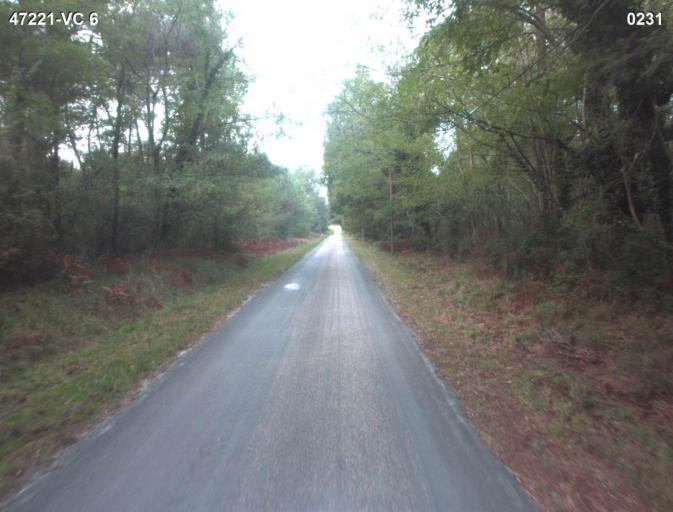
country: FR
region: Aquitaine
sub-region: Departement du Lot-et-Garonne
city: Mezin
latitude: 44.0974
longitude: 0.1769
